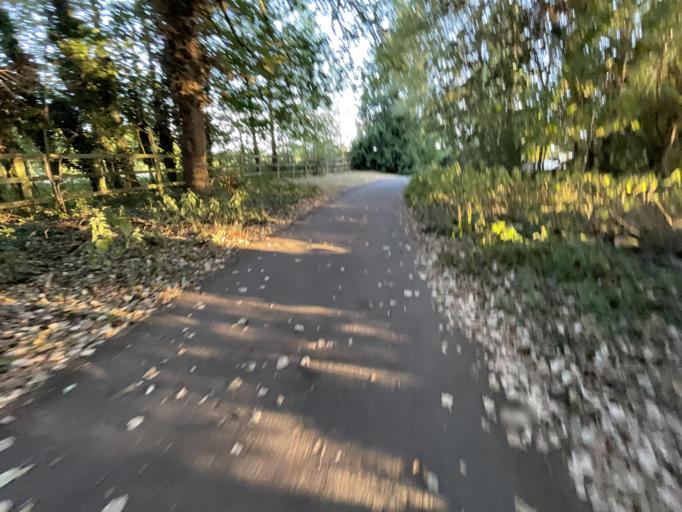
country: GB
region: England
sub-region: Surrey
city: East Horsley
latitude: 51.2664
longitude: -0.4248
